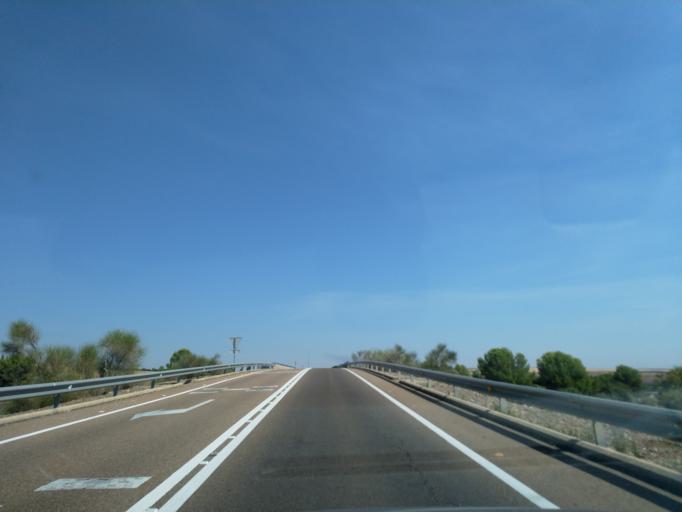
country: ES
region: Extremadura
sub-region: Provincia de Badajoz
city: Merida
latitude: 38.9412
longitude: -6.3432
